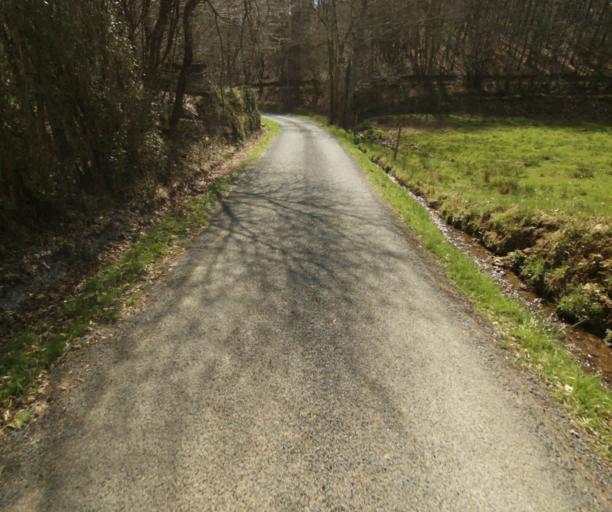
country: FR
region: Limousin
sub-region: Departement de la Correze
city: Seilhac
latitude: 45.4008
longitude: 1.7704
